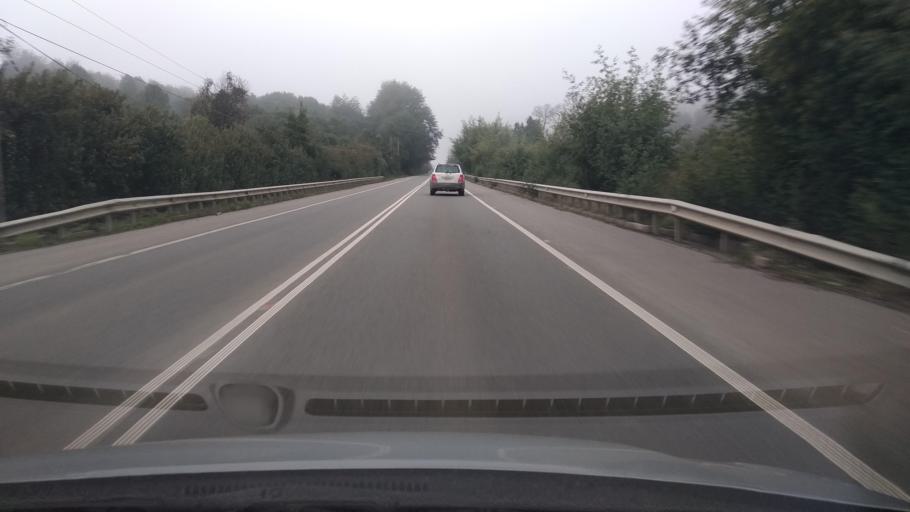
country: CL
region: Los Lagos
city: Las Animas
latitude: -39.7300
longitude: -73.1927
